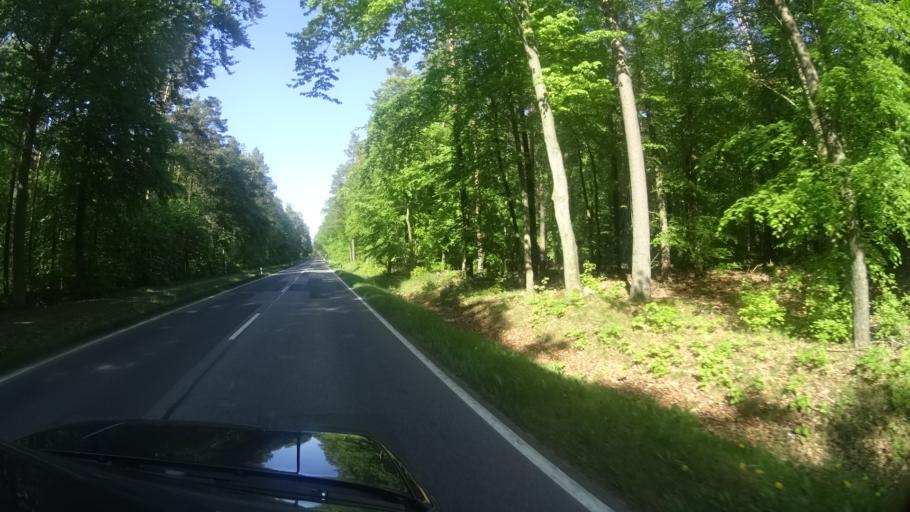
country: DE
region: Mecklenburg-Vorpommern
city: Seeheilbad Graal-Muritz
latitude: 54.2199
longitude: 12.2191
